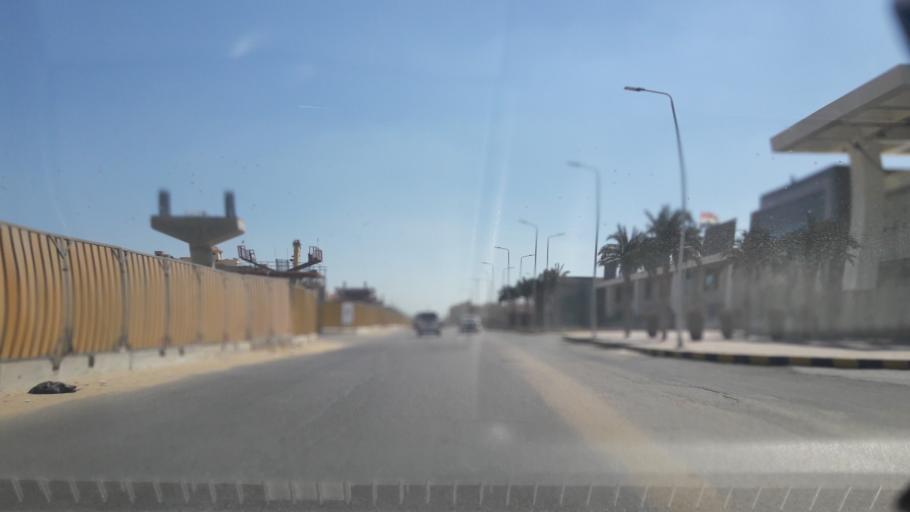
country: EG
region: Al Jizah
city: Madinat Sittah Uktubar
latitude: 29.9689
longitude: 30.9332
